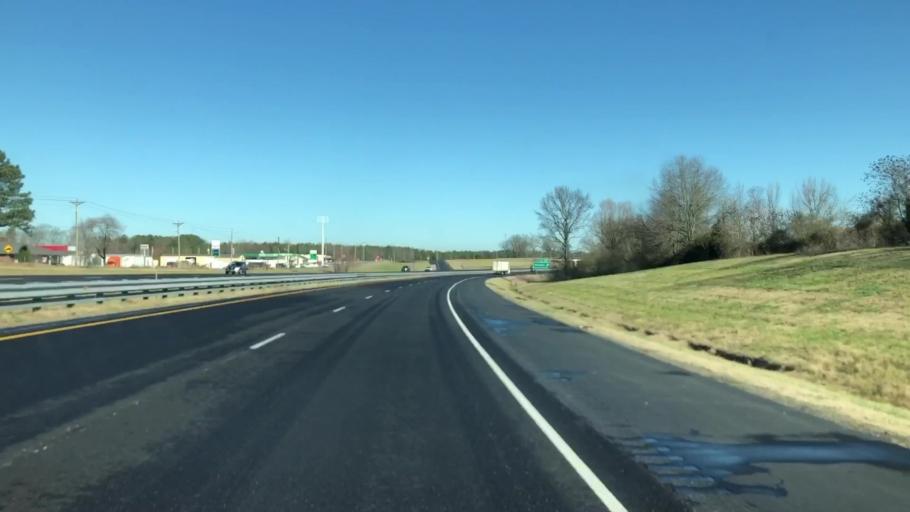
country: US
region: Alabama
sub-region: Limestone County
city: Ardmore
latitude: 34.9147
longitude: -86.9089
